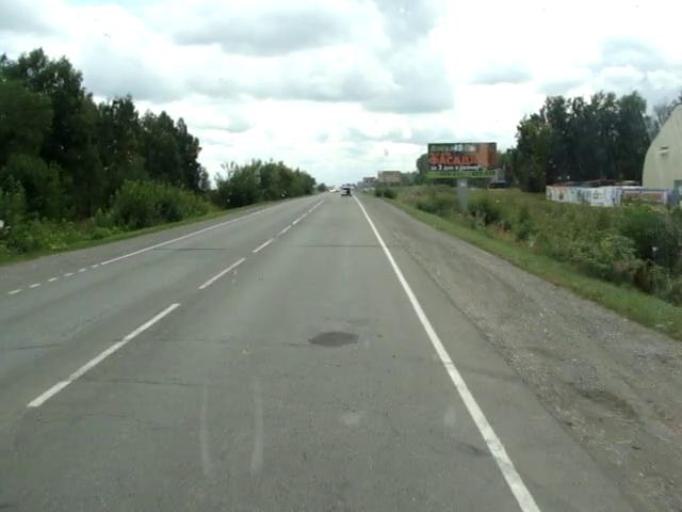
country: RU
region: Altai Krai
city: Zarya
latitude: 52.5744
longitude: 85.1811
